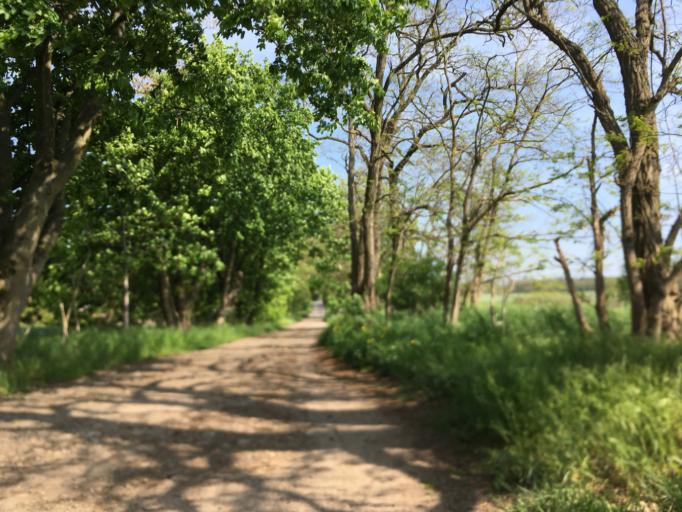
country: DE
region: Brandenburg
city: Altlandsberg
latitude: 52.5951
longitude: 13.7274
